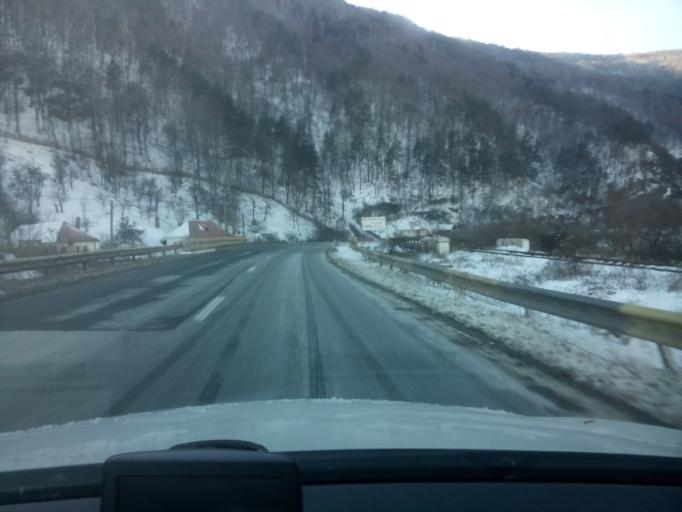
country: RO
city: Cainenii Mici
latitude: 45.4994
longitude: 24.2938
